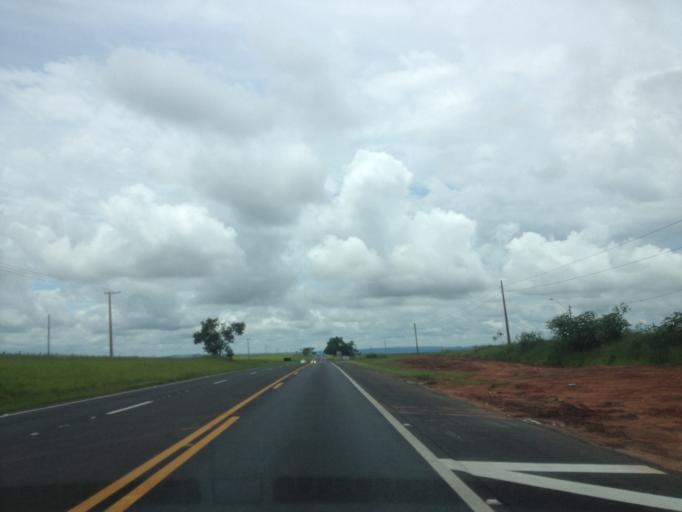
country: BR
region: Sao Paulo
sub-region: Marilia
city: Marilia
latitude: -22.2590
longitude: -49.9925
